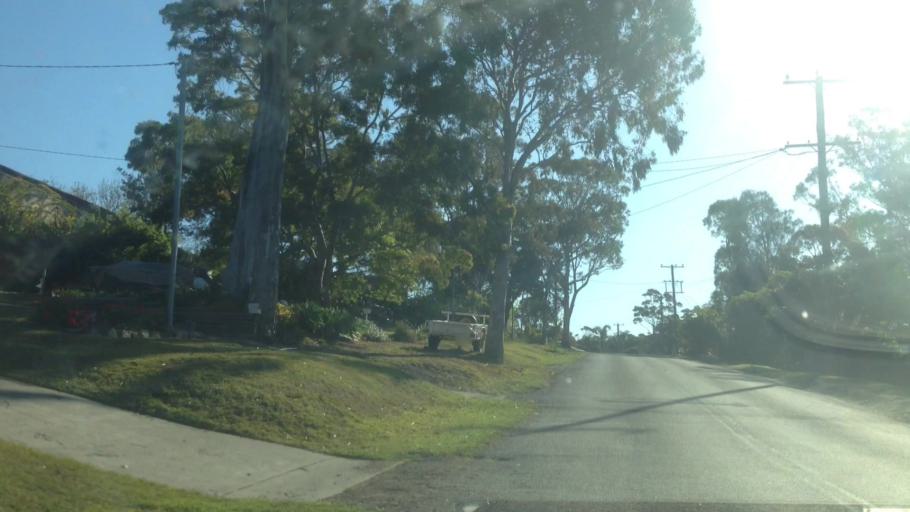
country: AU
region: New South Wales
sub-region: Lake Macquarie Shire
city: Arcadia vale
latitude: -33.1131
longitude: 151.5652
